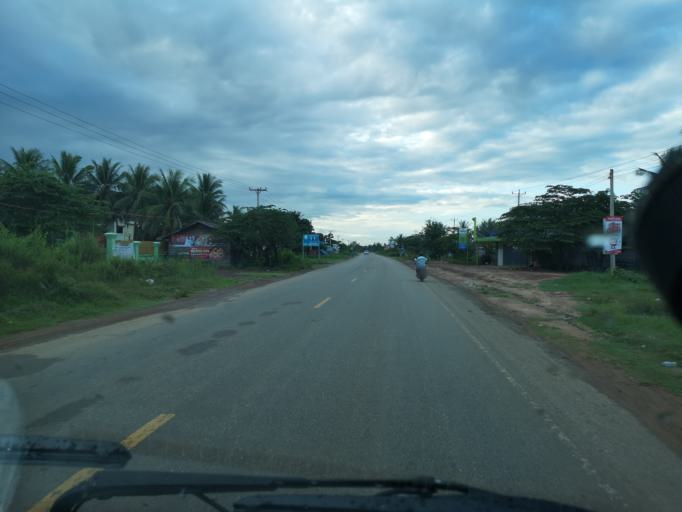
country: KH
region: Otar Meanchey
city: Samraong
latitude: 14.1637
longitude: 103.5184
